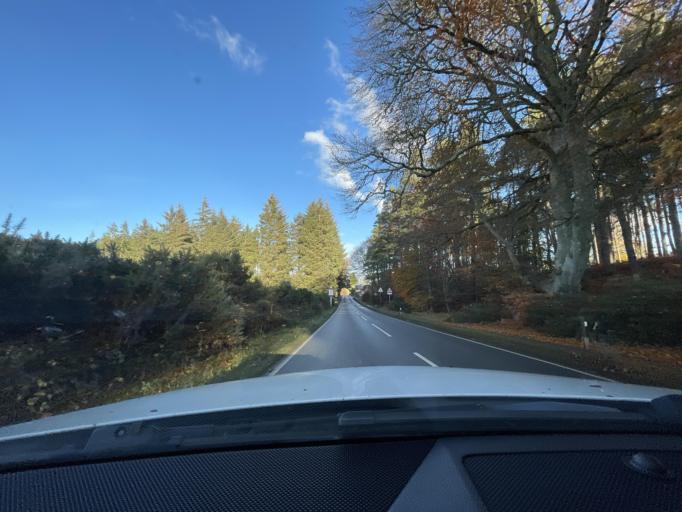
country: GB
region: Scotland
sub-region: Highland
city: Inverness
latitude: 57.3947
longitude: -4.3215
